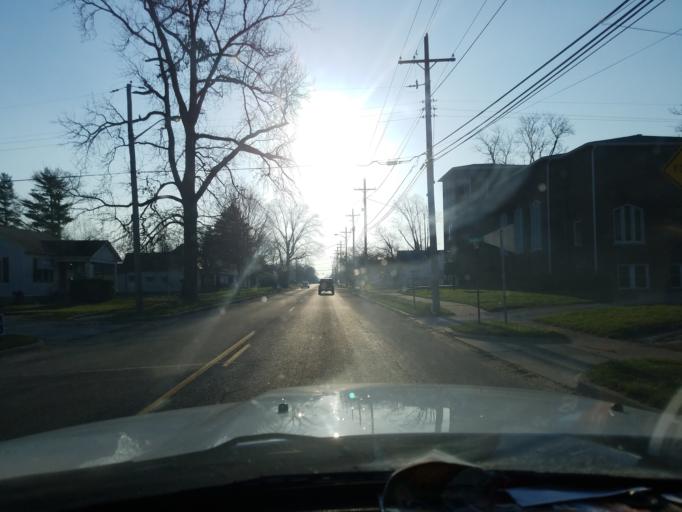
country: US
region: Indiana
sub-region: Vigo County
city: Seelyville
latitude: 39.3903
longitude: -87.3012
